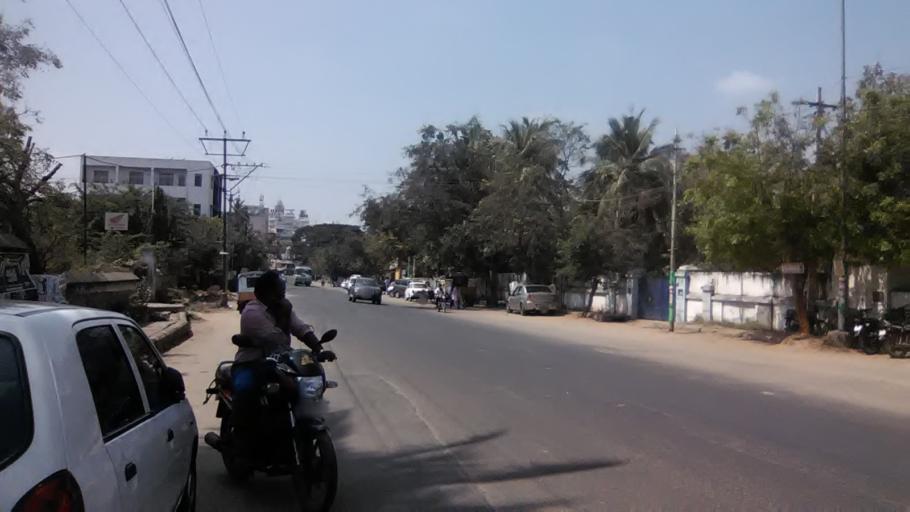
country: IN
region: Tamil Nadu
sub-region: Tiruchchirappalli
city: Tiruchirappalli
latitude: 10.8023
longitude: 78.6845
